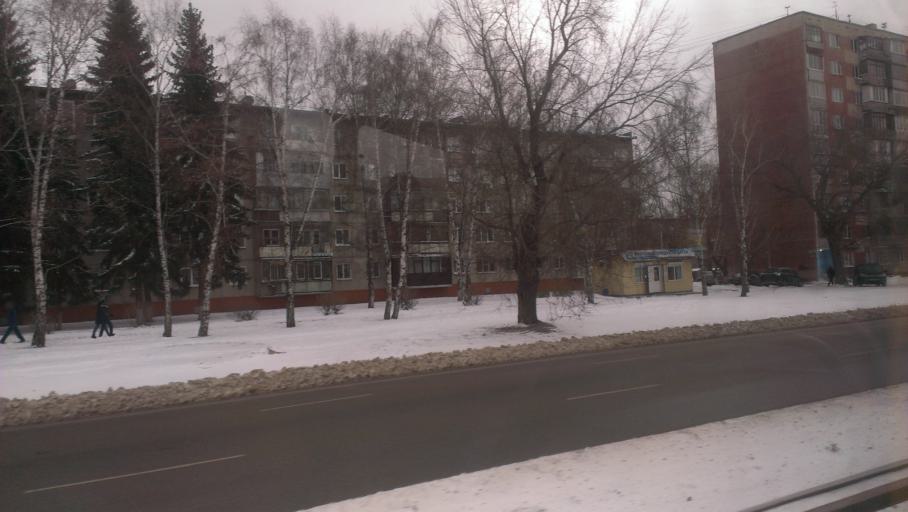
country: RU
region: Altai Krai
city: Novosilikatnyy
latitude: 53.3690
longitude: 83.6772
